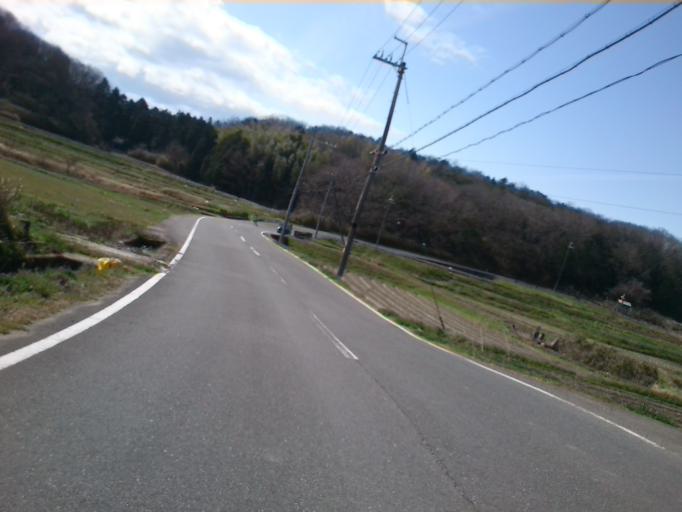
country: JP
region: Nara
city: Nara-shi
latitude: 34.7249
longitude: 135.8661
